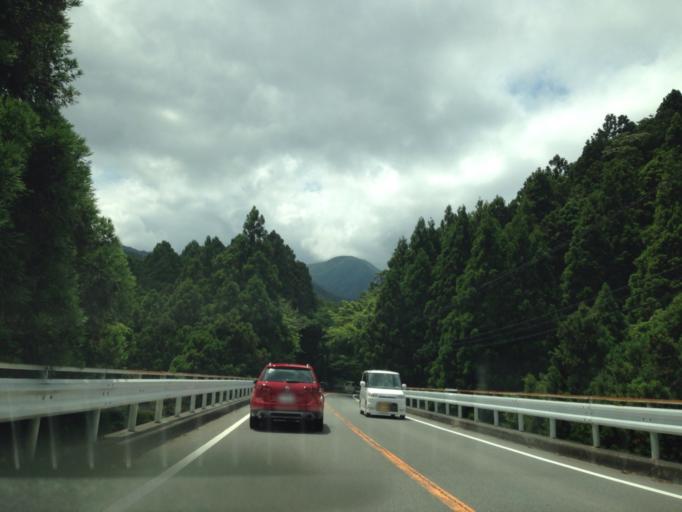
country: JP
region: Shizuoka
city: Heda
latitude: 34.9192
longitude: 138.8245
